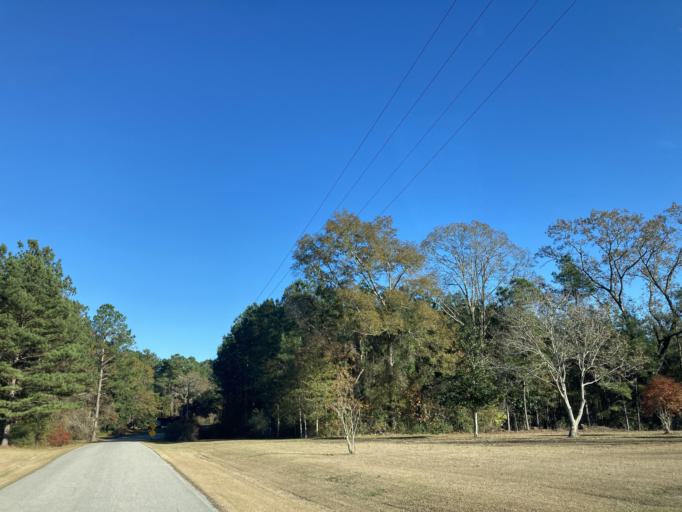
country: US
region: Mississippi
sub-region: Lamar County
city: Sumrall
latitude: 31.3658
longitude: -89.5667
